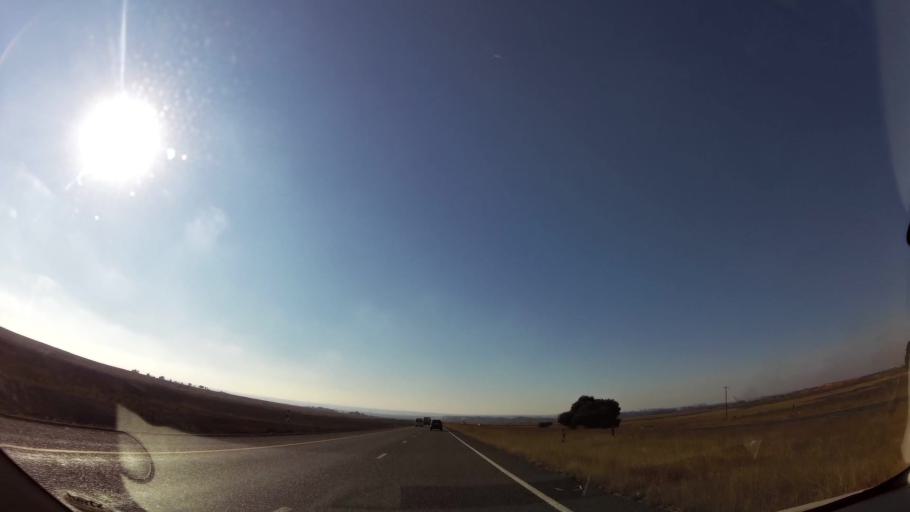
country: ZA
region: Mpumalanga
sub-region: Nkangala District Municipality
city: Witbank
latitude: -26.0186
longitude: 28.9847
